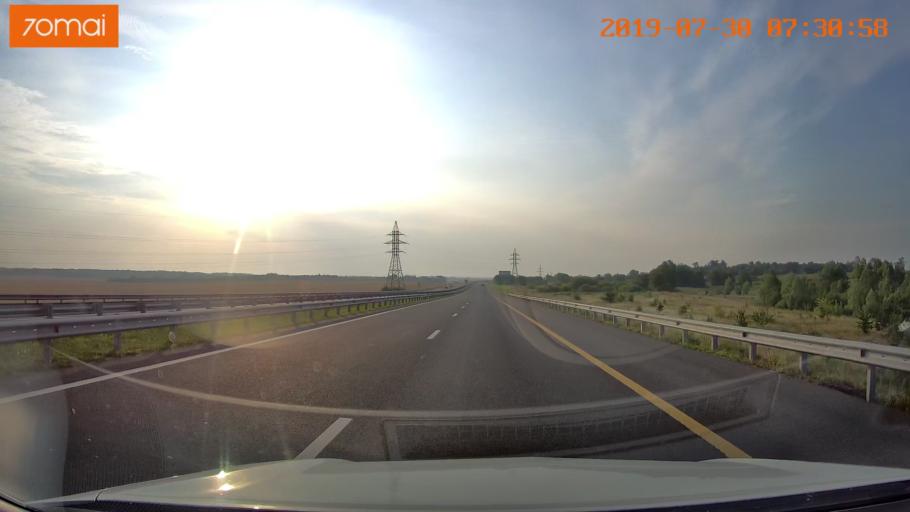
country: RU
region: Kaliningrad
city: Gvardeysk
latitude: 54.6692
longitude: 20.9787
